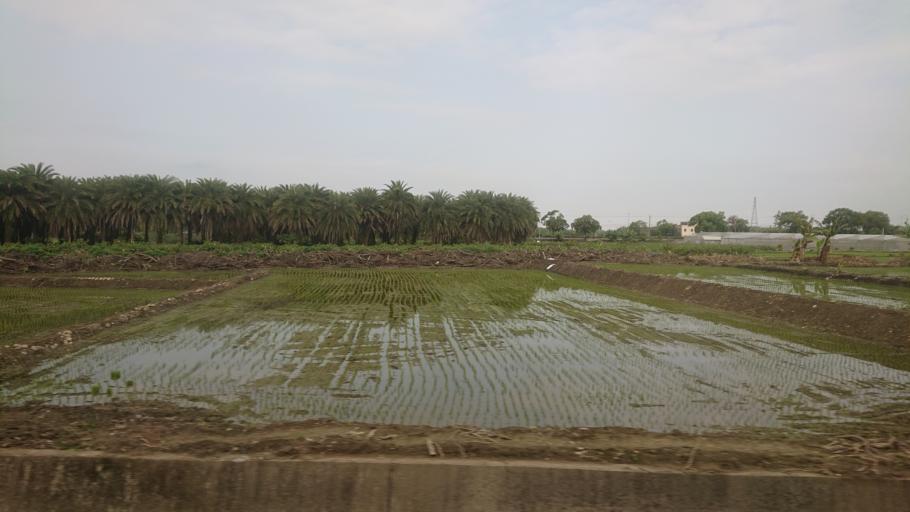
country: TW
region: Taiwan
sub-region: Yunlin
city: Douliu
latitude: 23.7627
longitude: 120.6183
